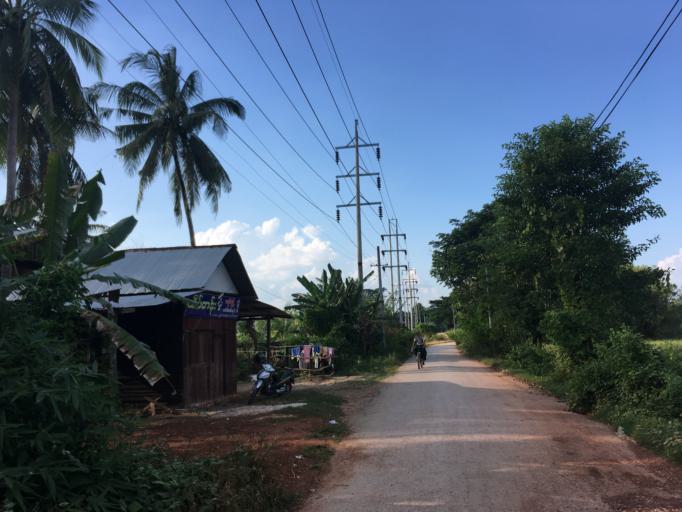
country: MM
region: Mon
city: Mawlamyine
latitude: 16.4299
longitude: 97.6223
